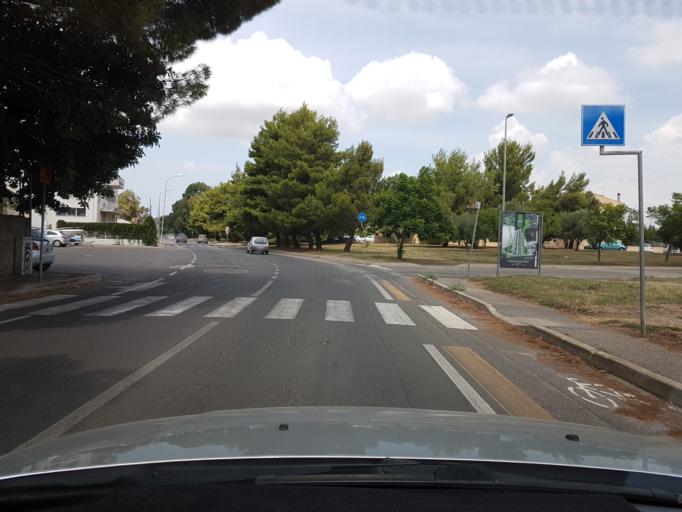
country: IT
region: Sardinia
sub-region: Provincia di Oristano
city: Oristano
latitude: 39.9127
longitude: 8.5900
